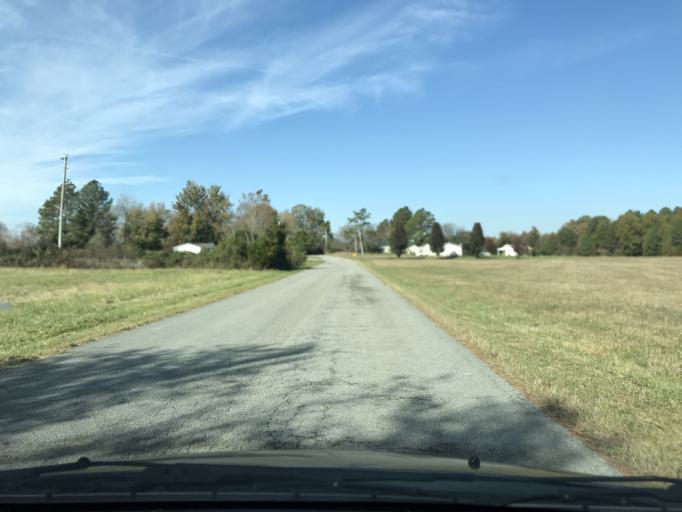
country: US
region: Tennessee
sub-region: Coffee County
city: Tullahoma
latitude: 35.4067
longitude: -86.1585
